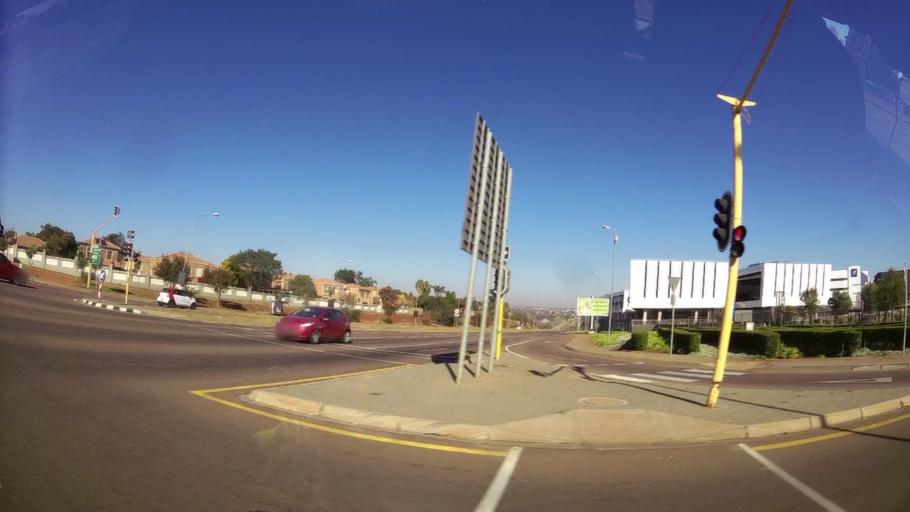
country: ZA
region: Gauteng
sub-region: City of Tshwane Metropolitan Municipality
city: Centurion
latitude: -25.8639
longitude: 28.2106
